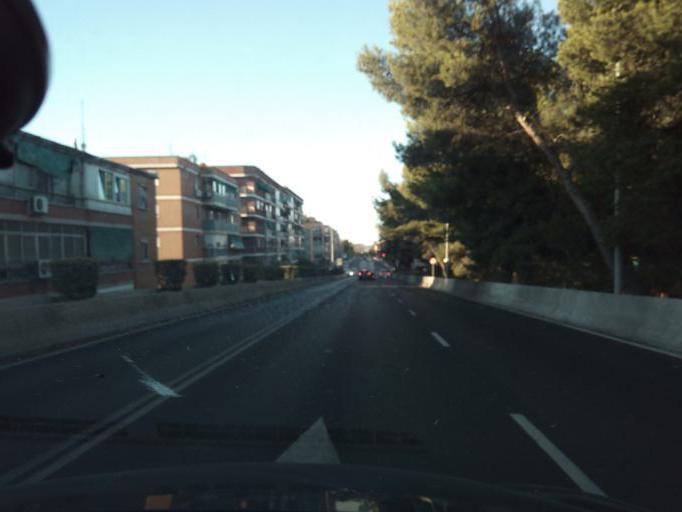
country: ES
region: Madrid
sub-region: Provincia de Madrid
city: Torrejon de Ardoz
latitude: 40.4629
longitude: -3.4841
